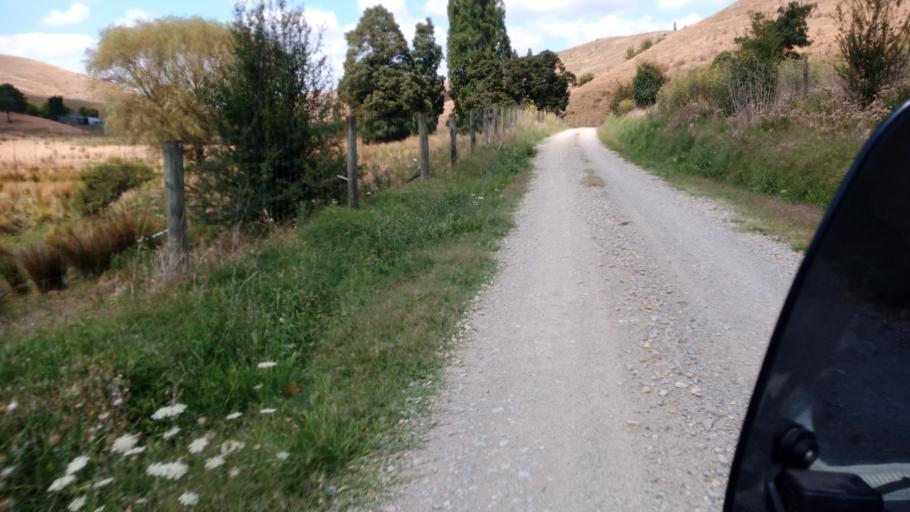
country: NZ
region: Gisborne
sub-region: Gisborne District
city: Gisborne
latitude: -38.4773
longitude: 177.8266
